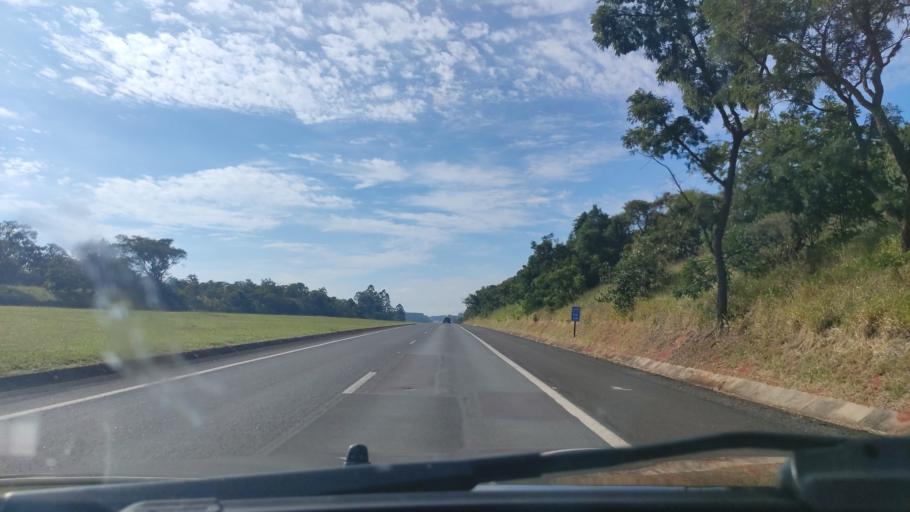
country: BR
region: Sao Paulo
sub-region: Itatinga
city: Itatinga
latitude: -23.0485
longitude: -48.6008
